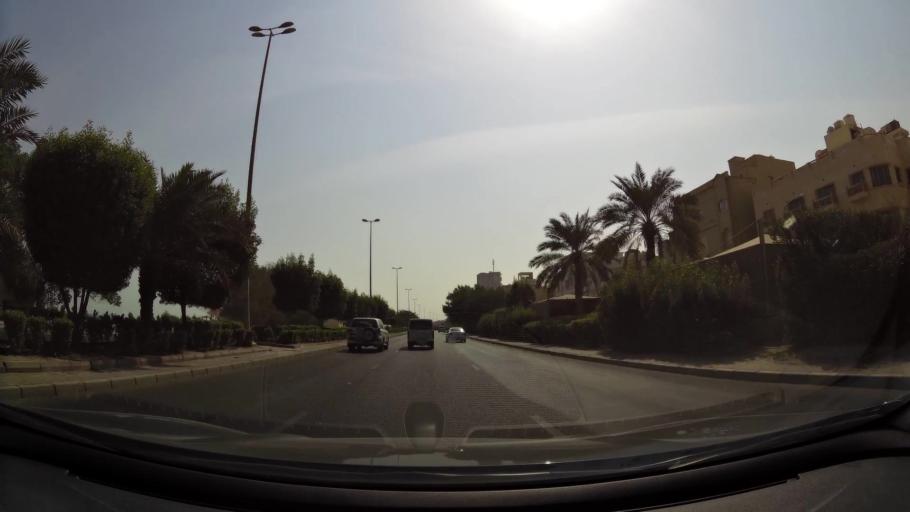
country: KW
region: Al Ahmadi
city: Al Manqaf
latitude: 29.1068
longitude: 48.1370
